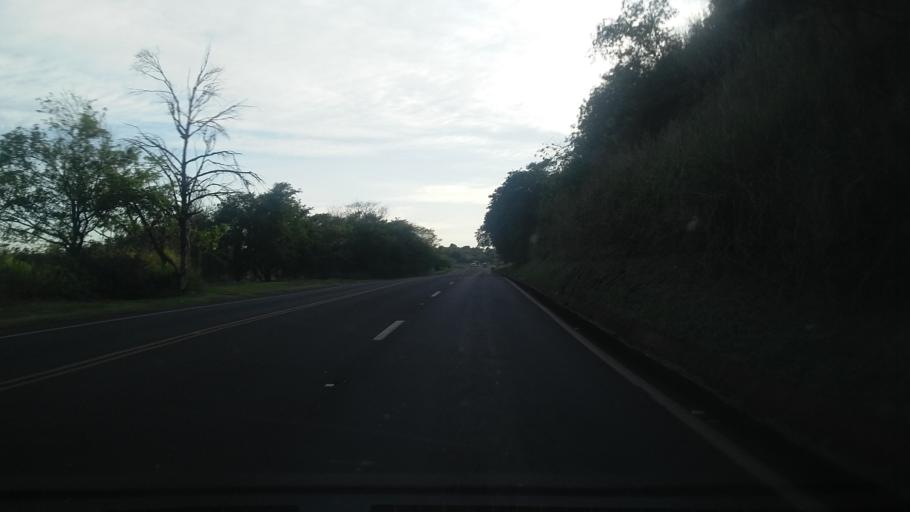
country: BR
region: Parana
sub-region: Assai
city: Assai
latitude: -23.2082
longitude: -50.6613
